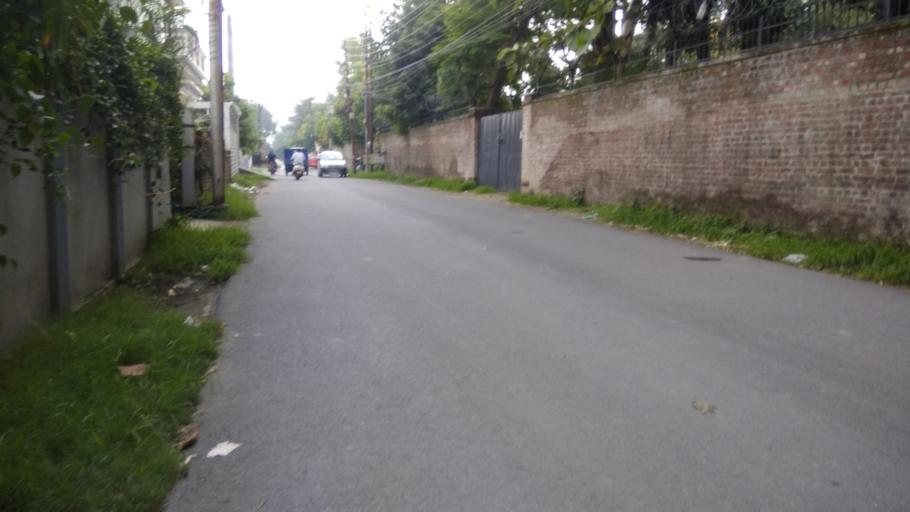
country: IN
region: Uttarakhand
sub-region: Dehradun
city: Dehradun
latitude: 30.3150
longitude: 78.0574
